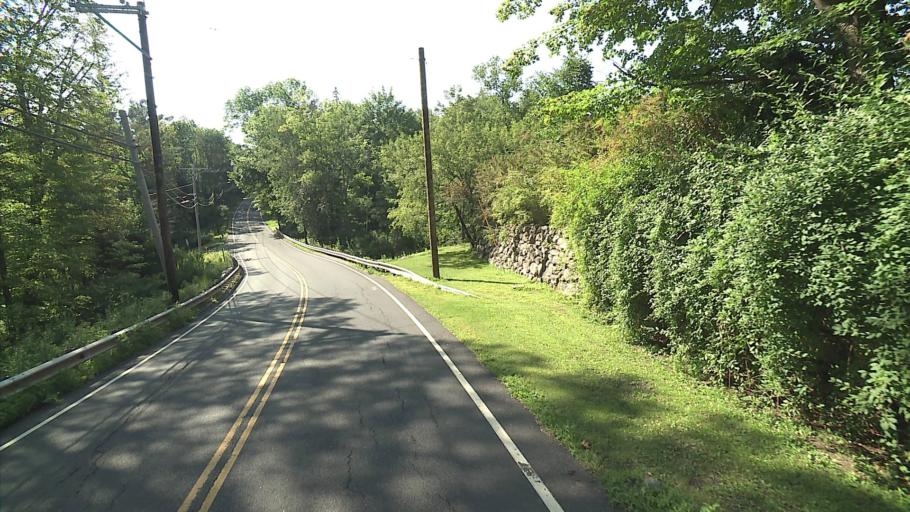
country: US
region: Connecticut
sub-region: Litchfield County
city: Winsted
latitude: 41.9918
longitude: -73.0982
